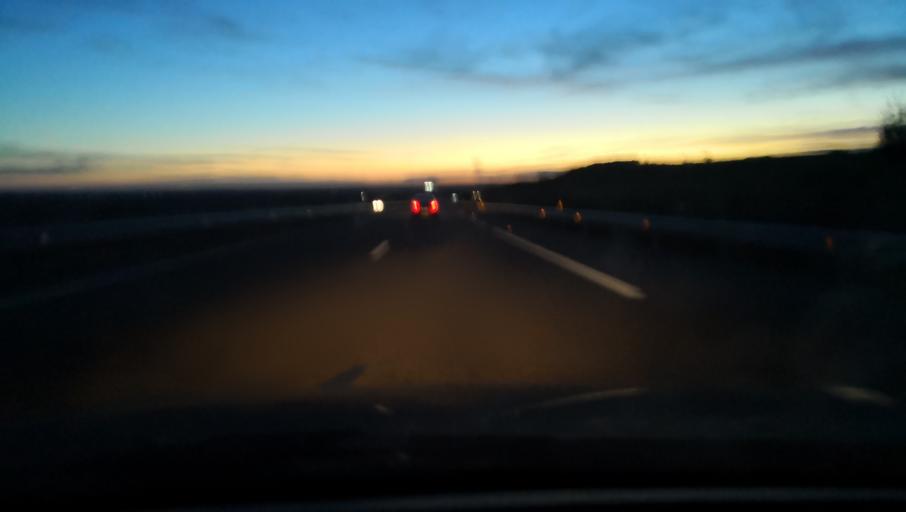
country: ES
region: Castille and Leon
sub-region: Provincia de Zamora
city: Coreses
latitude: 41.5478
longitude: -5.6479
